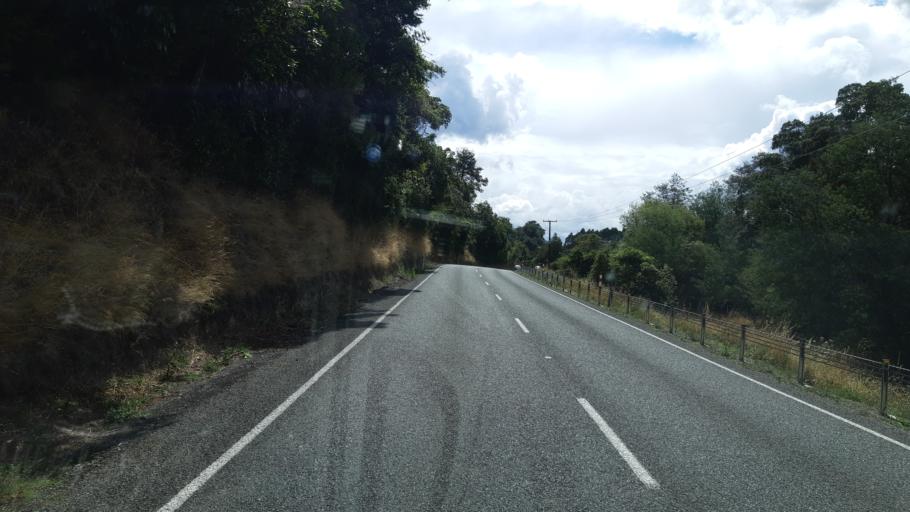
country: NZ
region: Tasman
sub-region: Tasman District
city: Wakefield
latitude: -41.4992
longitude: 172.7953
